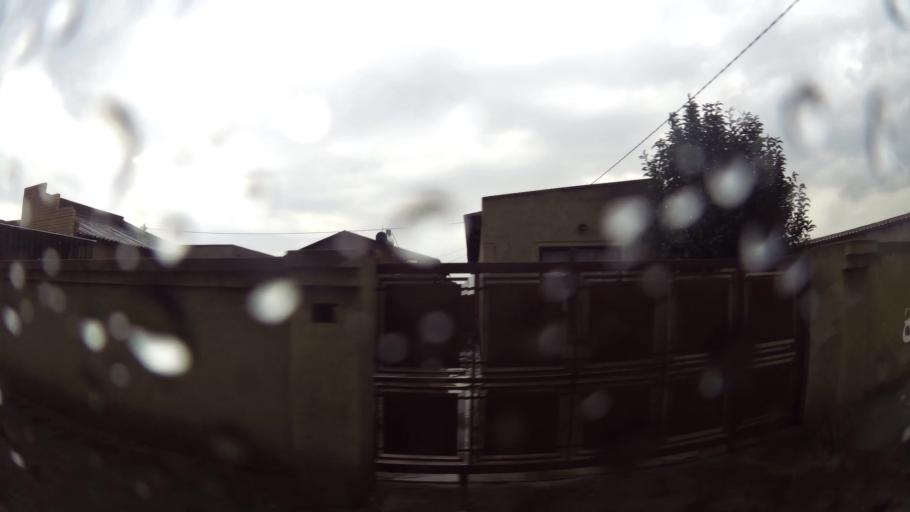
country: ZA
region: Gauteng
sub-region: Ekurhuleni Metropolitan Municipality
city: Germiston
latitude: -26.3735
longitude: 28.1500
